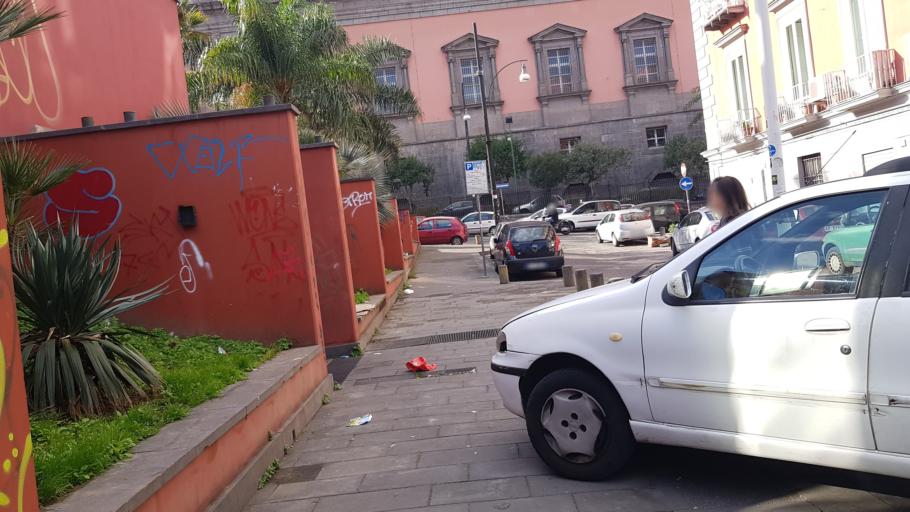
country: IT
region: Campania
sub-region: Provincia di Napoli
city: Napoli
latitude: 40.8539
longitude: 14.2521
